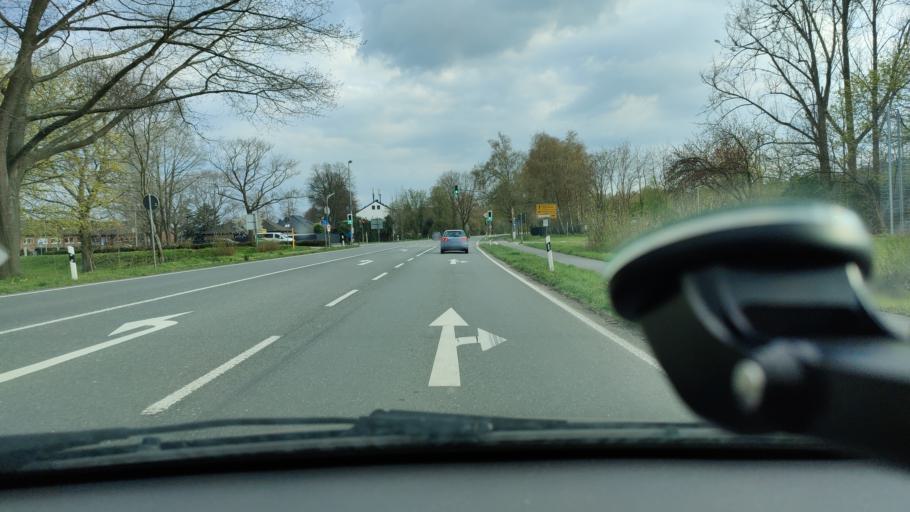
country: DE
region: North Rhine-Westphalia
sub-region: Regierungsbezirk Dusseldorf
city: Wesel
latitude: 51.6954
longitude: 6.6055
